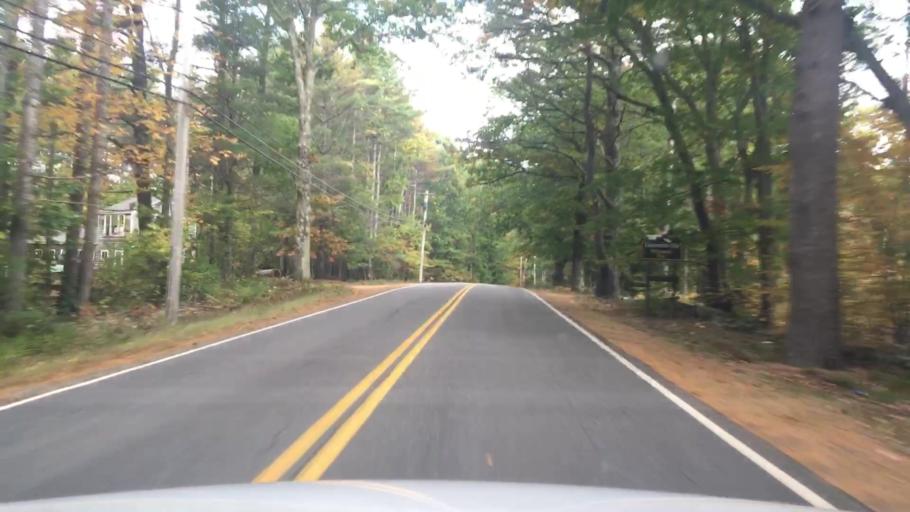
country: US
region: Maine
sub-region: Knox County
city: Hope
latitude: 44.2658
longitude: -69.1346
